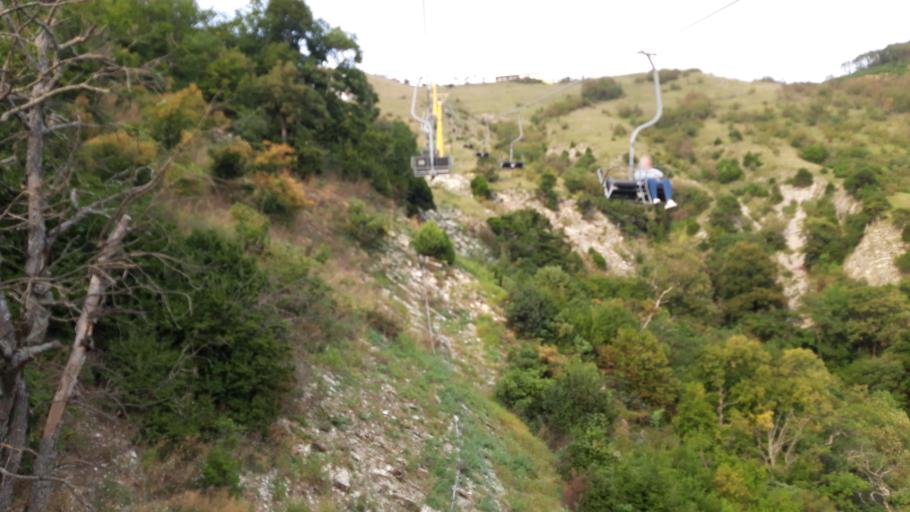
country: RU
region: Krasnodarskiy
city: Gelendzhik
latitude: 44.5820
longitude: 38.0980
